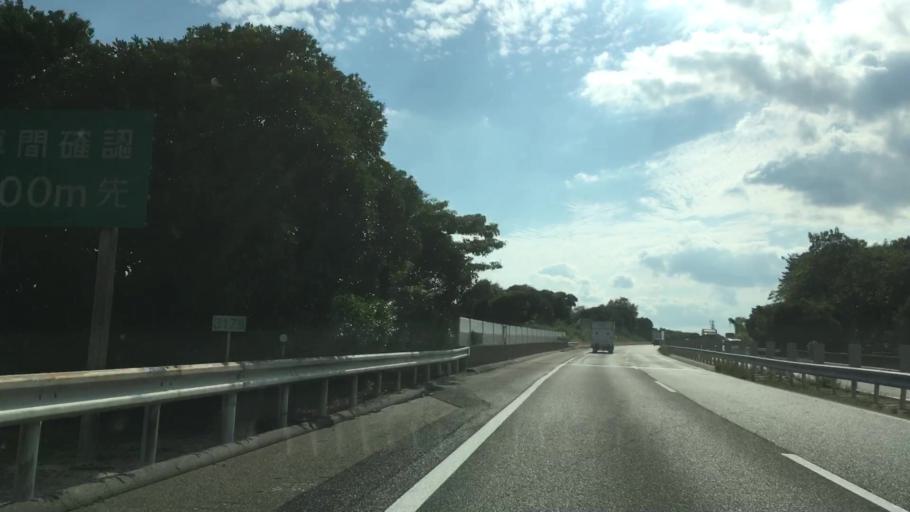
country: JP
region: Hiroshima
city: Ono-hara
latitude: 34.2776
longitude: 132.2562
